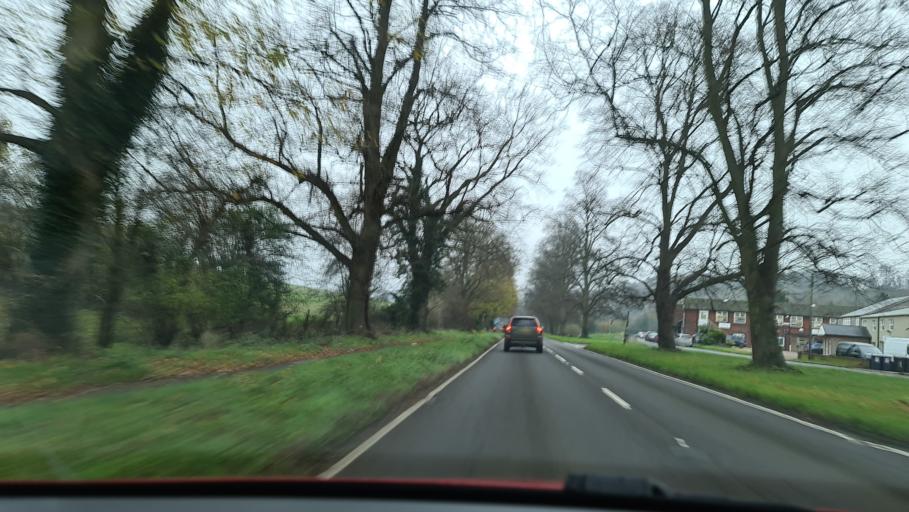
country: GB
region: England
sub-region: Buckinghamshire
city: Stokenchurch
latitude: 51.6415
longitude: -0.8327
